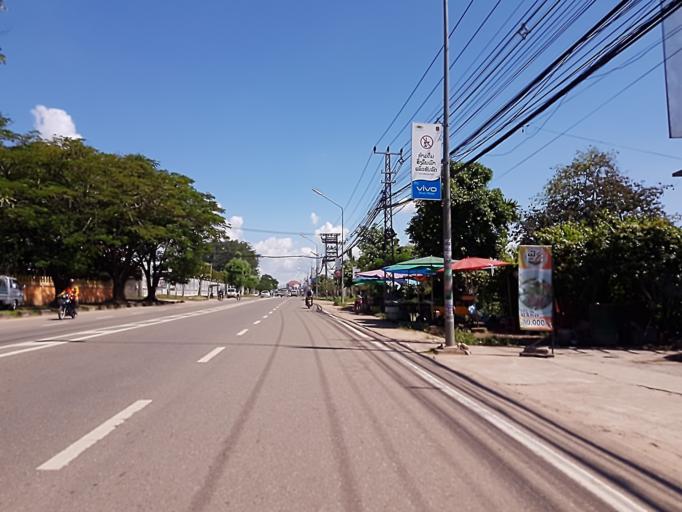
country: TH
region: Nong Khai
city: Si Chiang Mai
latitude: 17.9025
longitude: 102.6306
